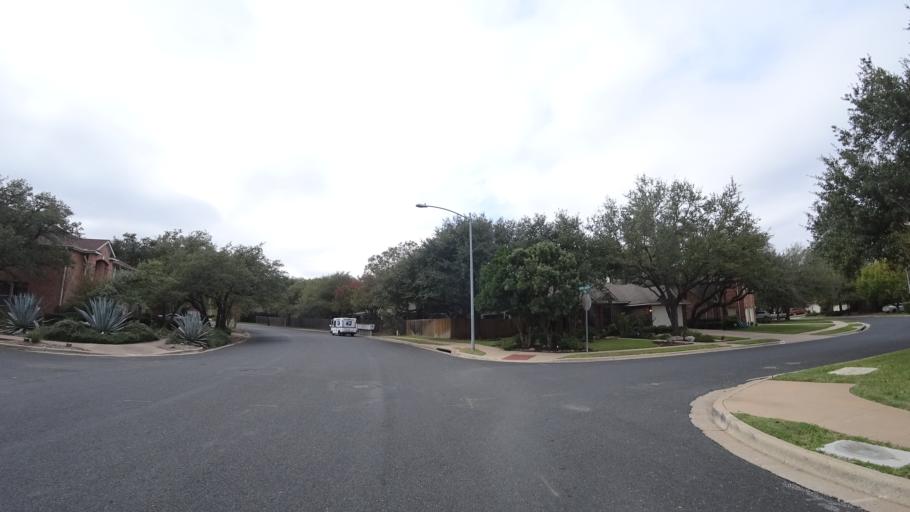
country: US
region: Texas
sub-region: Travis County
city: Shady Hollow
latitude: 30.2212
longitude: -97.8740
